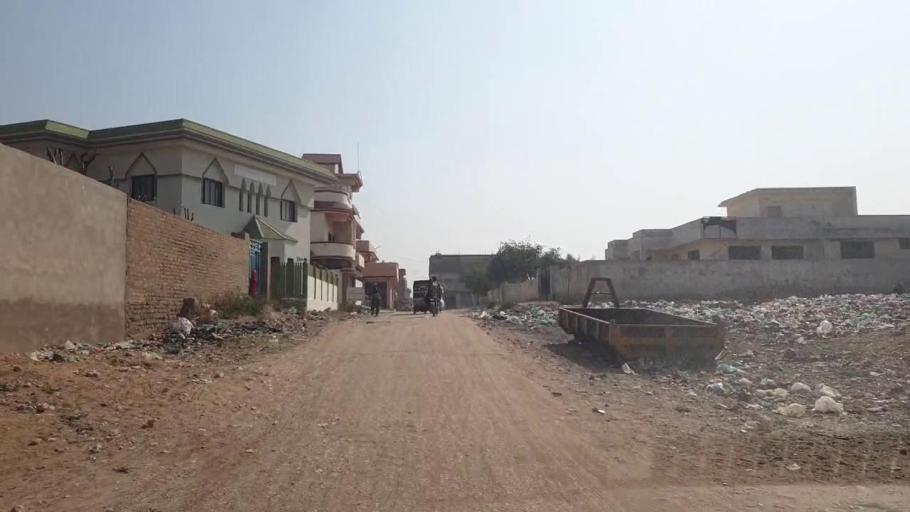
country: PK
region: Sindh
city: Kotri
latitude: 25.3458
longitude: 68.2810
